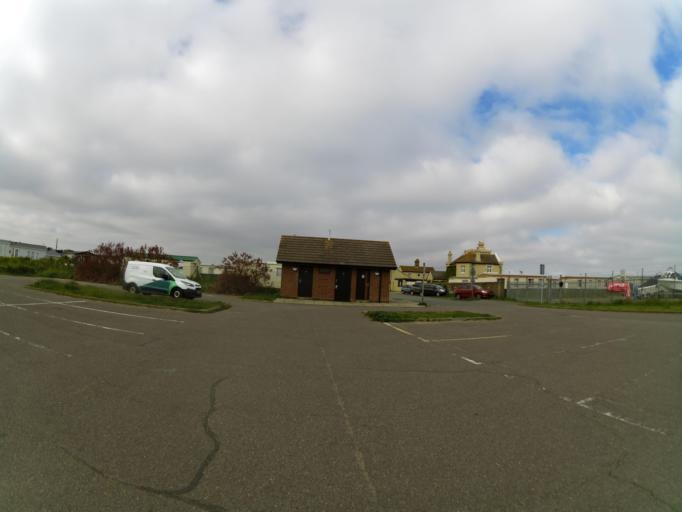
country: GB
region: England
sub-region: Suffolk
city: Felixstowe
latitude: 51.9445
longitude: 1.3303
